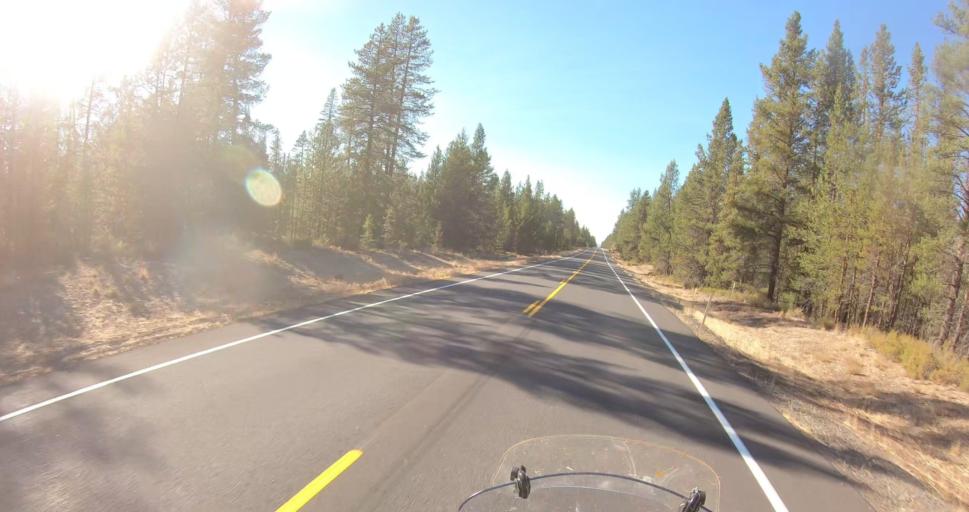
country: US
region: Oregon
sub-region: Deschutes County
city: La Pine
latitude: 43.4773
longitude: -121.4109
